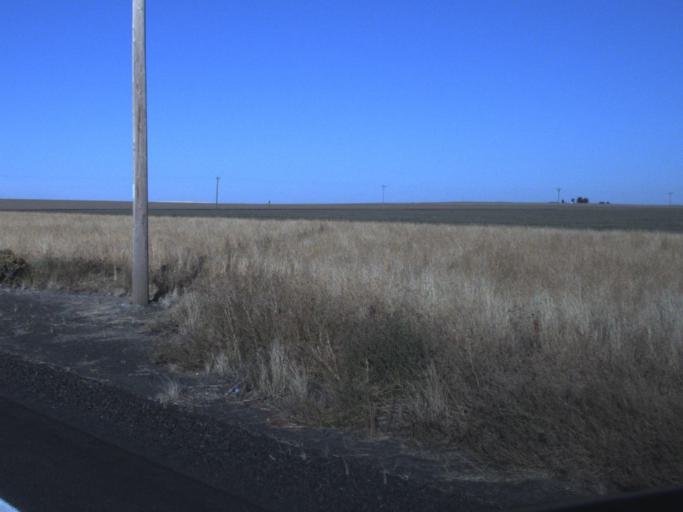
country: US
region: Washington
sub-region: Adams County
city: Ritzville
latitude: 46.9549
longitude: -118.3434
